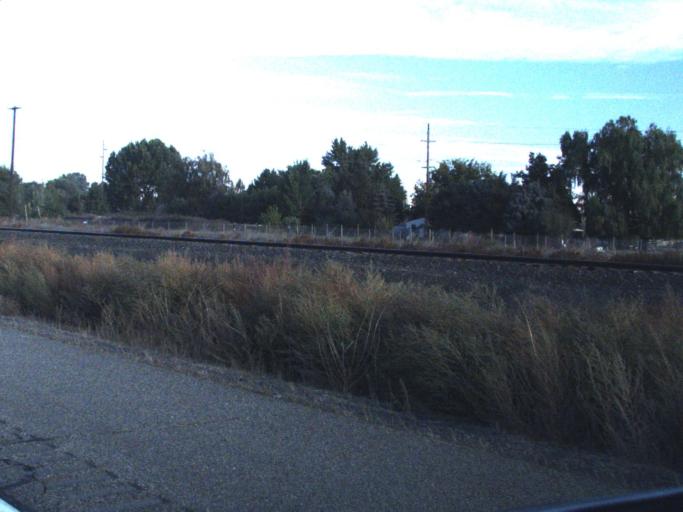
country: US
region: Washington
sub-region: Yakima County
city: Sunnyside
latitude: 46.2932
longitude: -119.9540
